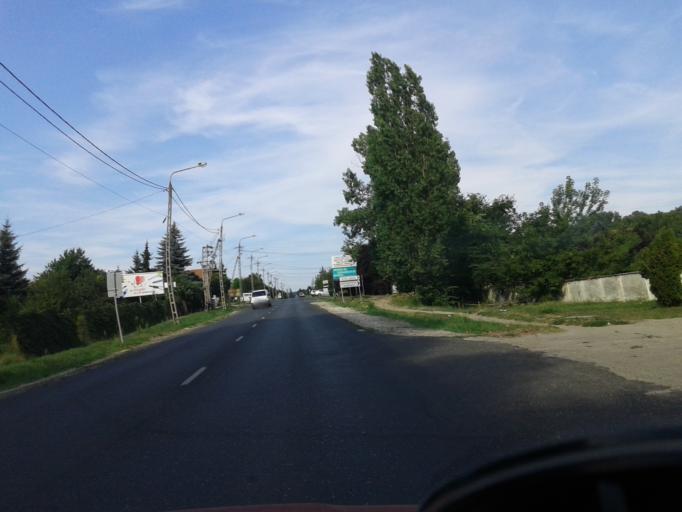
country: HU
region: Pest
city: Kerepes
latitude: 47.5554
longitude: 19.2756
